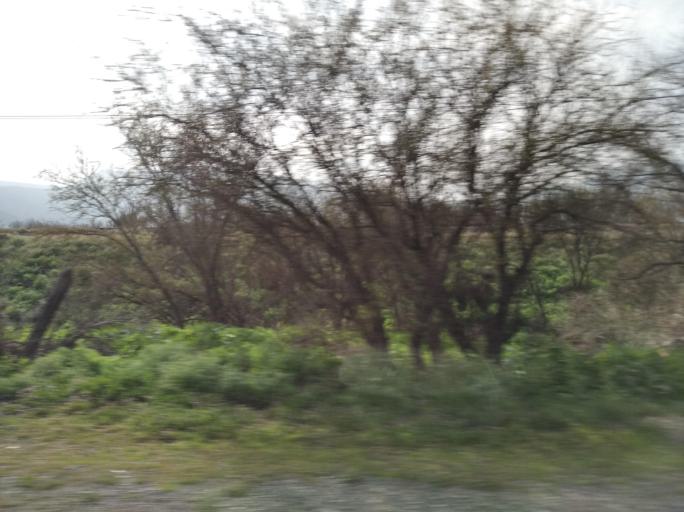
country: CL
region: Santiago Metropolitan
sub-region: Provincia de Chacabuco
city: Lampa
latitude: -33.1264
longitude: -70.9230
